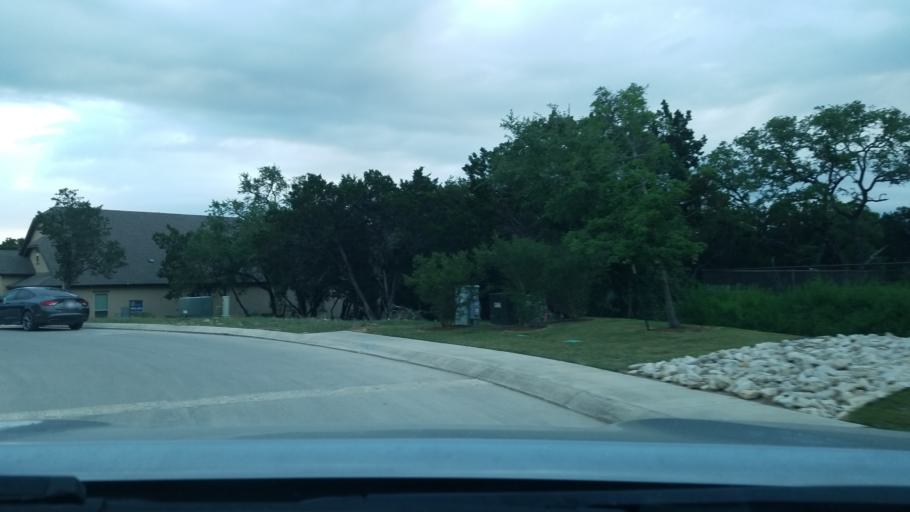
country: US
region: Texas
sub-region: Bexar County
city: Timberwood Park
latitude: 29.7171
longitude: -98.4575
